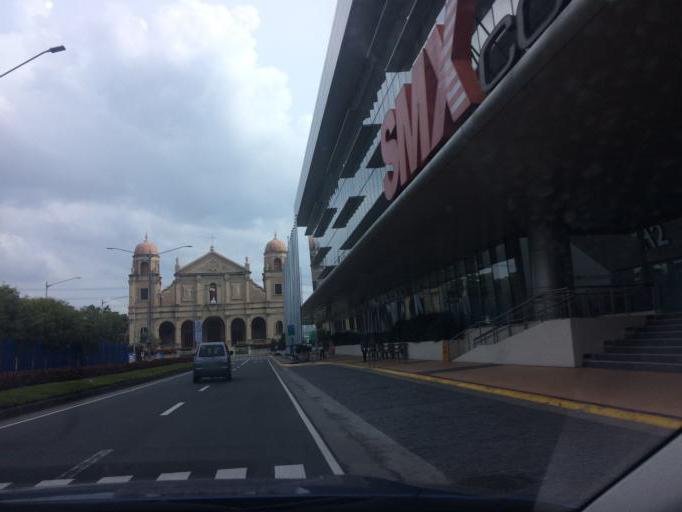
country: PH
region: Metro Manila
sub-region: City of Manila
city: Port Area
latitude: 14.5321
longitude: 120.9819
